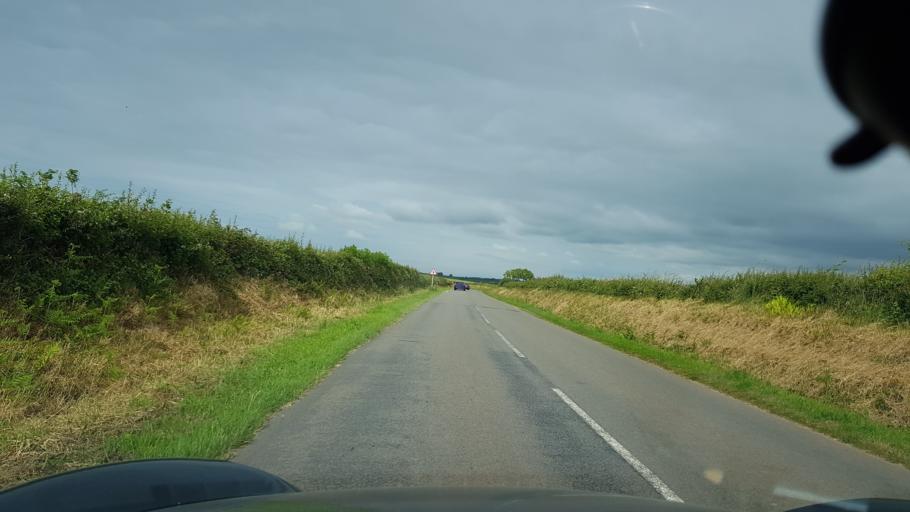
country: GB
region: Wales
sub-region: Pembrokeshire
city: Dale
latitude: 51.7449
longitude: -5.1475
